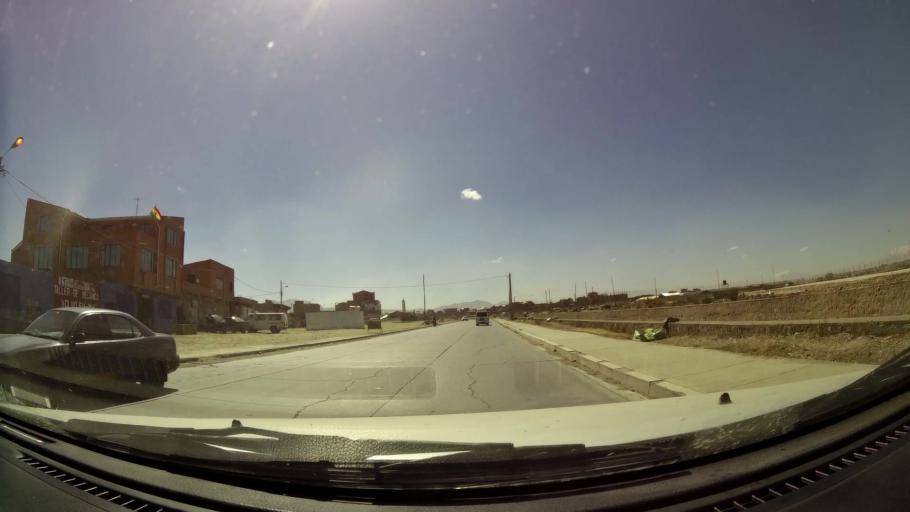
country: BO
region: La Paz
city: La Paz
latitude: -16.5114
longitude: -68.2152
